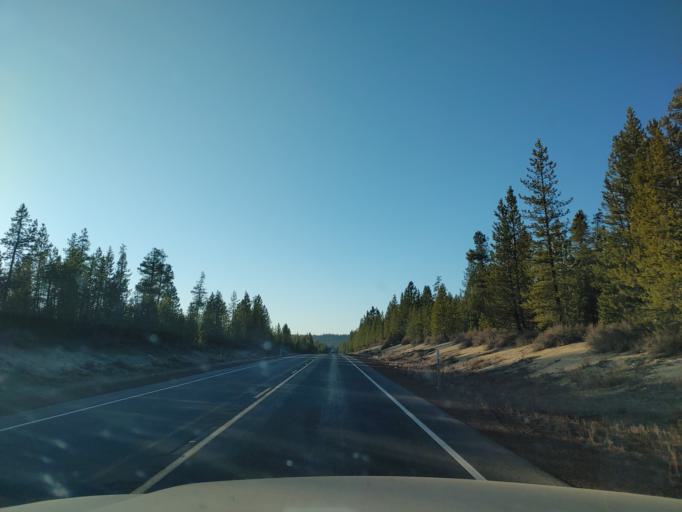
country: US
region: Oregon
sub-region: Deschutes County
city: La Pine
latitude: 43.4244
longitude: -121.8457
